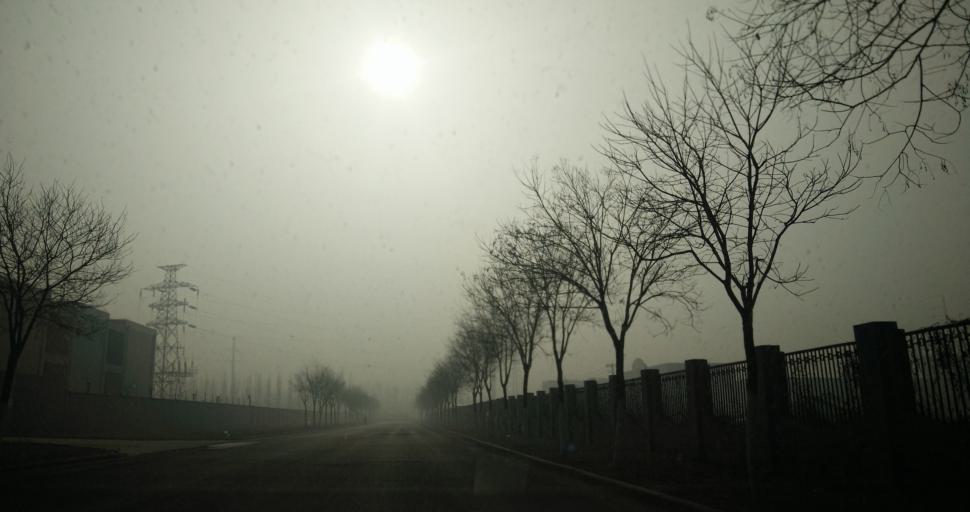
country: CN
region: Beijing
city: Yinghai
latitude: 39.7425
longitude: 116.4432
